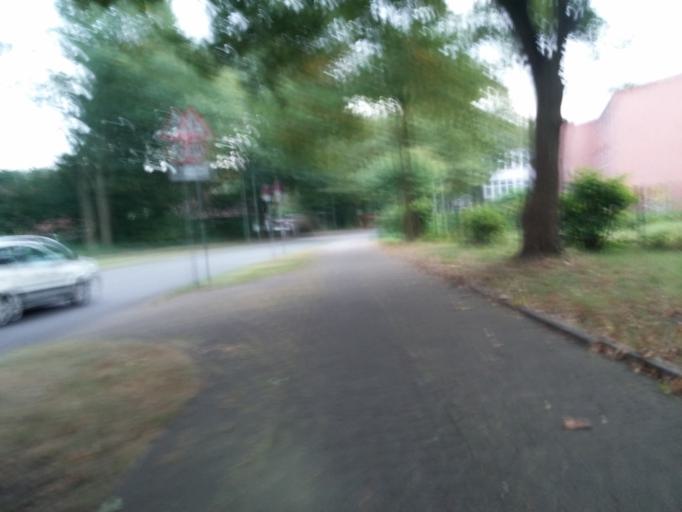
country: DE
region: North Rhine-Westphalia
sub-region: Regierungsbezirk Munster
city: Gladbeck
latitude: 51.6040
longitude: 7.0424
